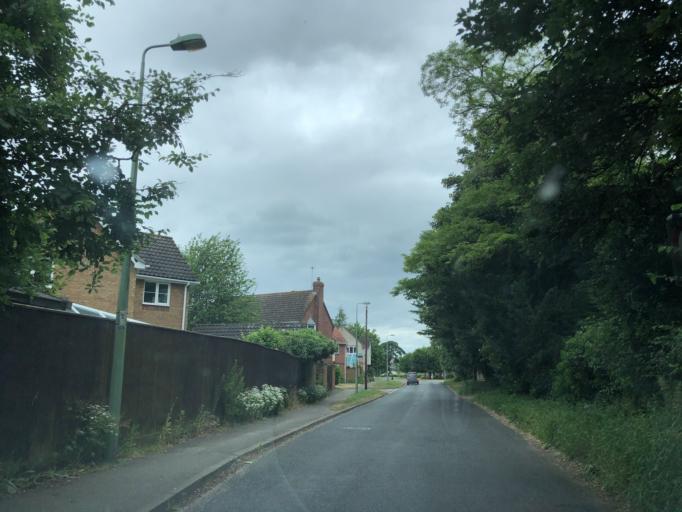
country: GB
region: England
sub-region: Suffolk
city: Thurston
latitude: 52.2496
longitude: 0.8144
